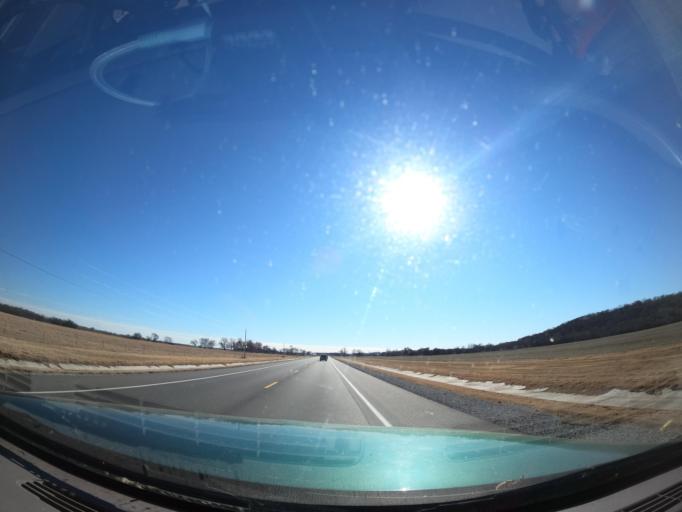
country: US
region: Oklahoma
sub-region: Wagoner County
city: Coweta
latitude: 35.8986
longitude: -95.6592
